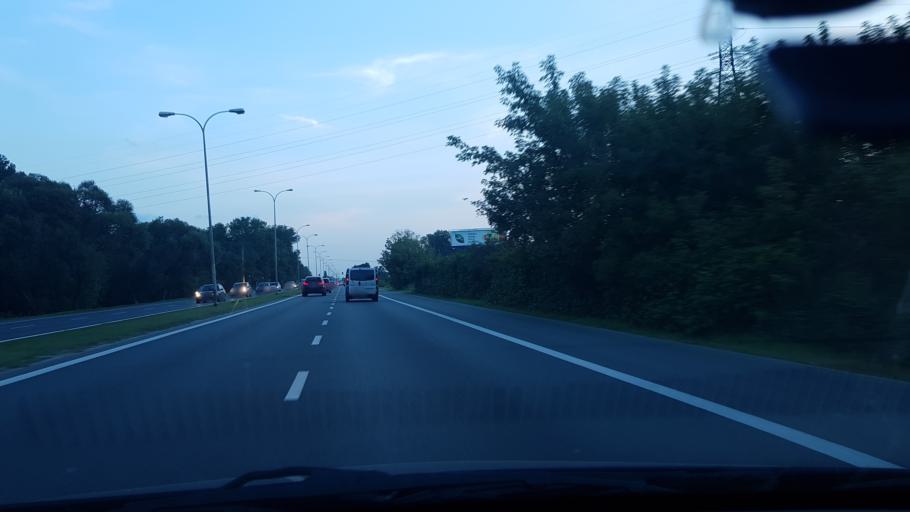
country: PL
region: Masovian Voivodeship
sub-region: Powiat wolominski
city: Zabki
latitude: 52.2972
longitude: 21.0838
